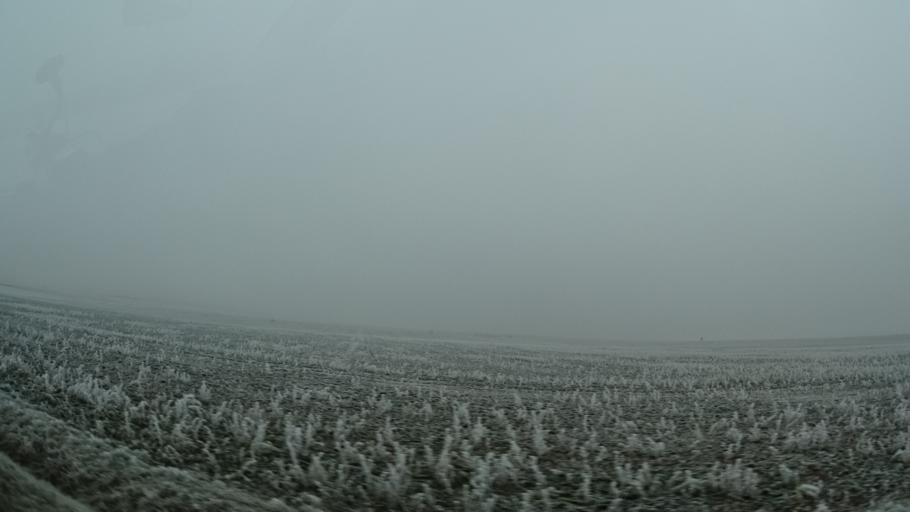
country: DE
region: Thuringia
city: Henneberg
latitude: 50.5179
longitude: 10.3060
